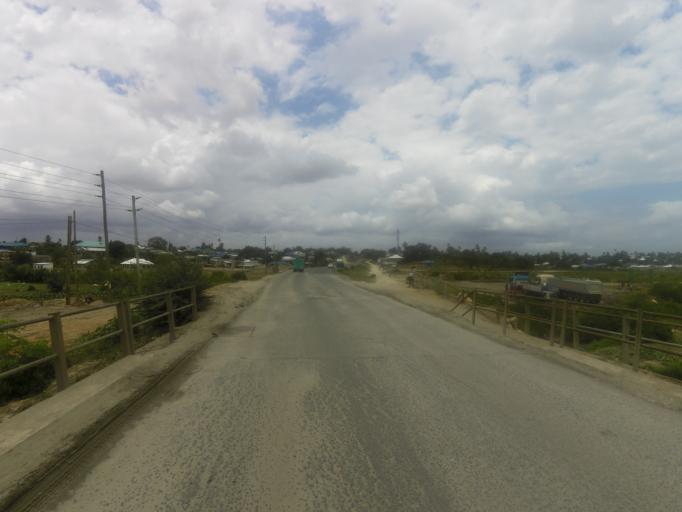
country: TZ
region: Pwani
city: Vikindu
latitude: -6.9369
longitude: 39.2746
